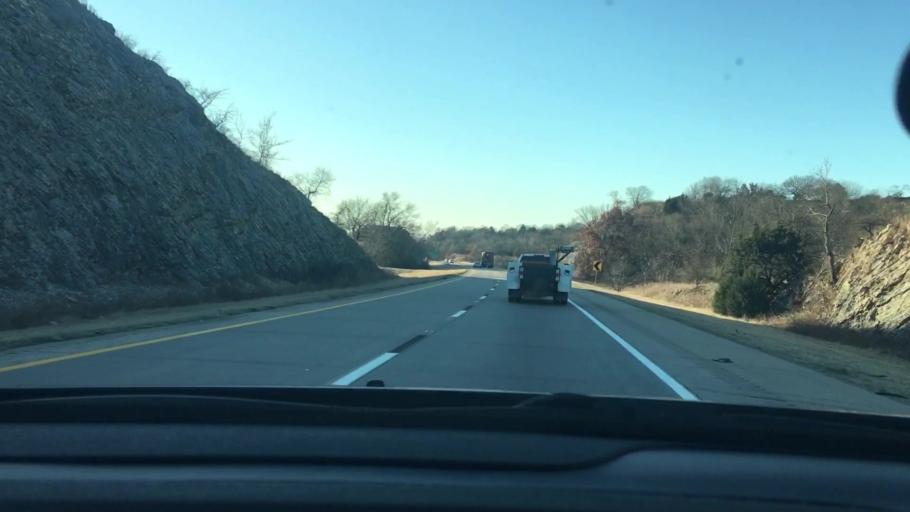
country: US
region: Oklahoma
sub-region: Murray County
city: Davis
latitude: 34.3581
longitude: -97.1490
